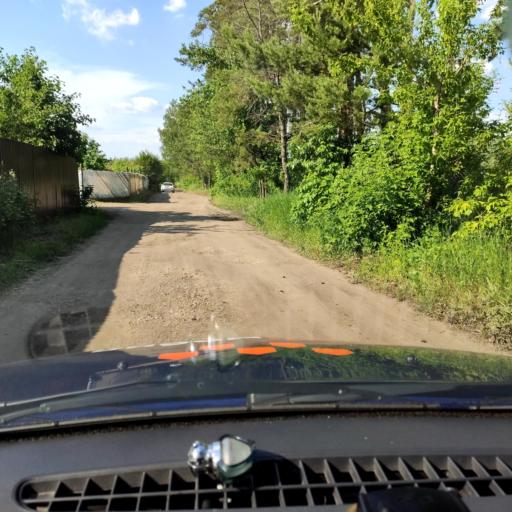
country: RU
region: Voronezj
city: Ramon'
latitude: 51.8927
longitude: 39.2067
